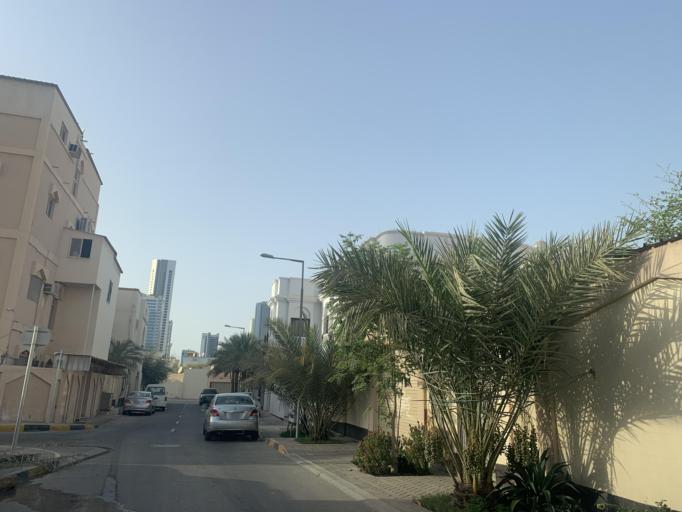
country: BH
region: Manama
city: Jidd Hafs
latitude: 26.2242
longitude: 50.5485
